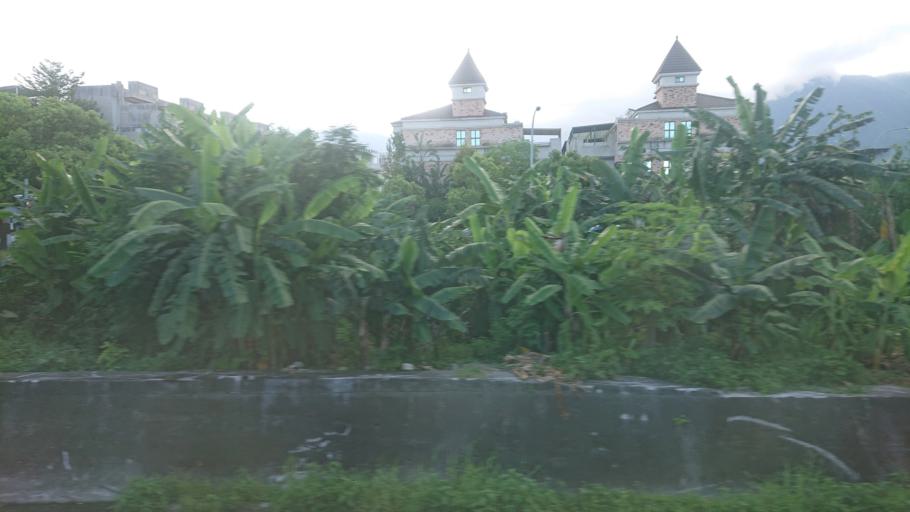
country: TW
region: Taiwan
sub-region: Hualien
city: Hualian
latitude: 23.9789
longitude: 121.5941
